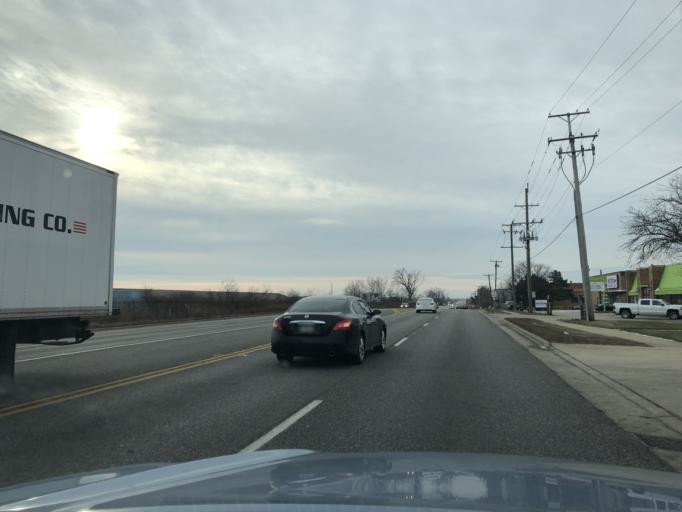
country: US
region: Illinois
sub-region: Cook County
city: Elk Grove Village
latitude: 41.9928
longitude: -87.9400
